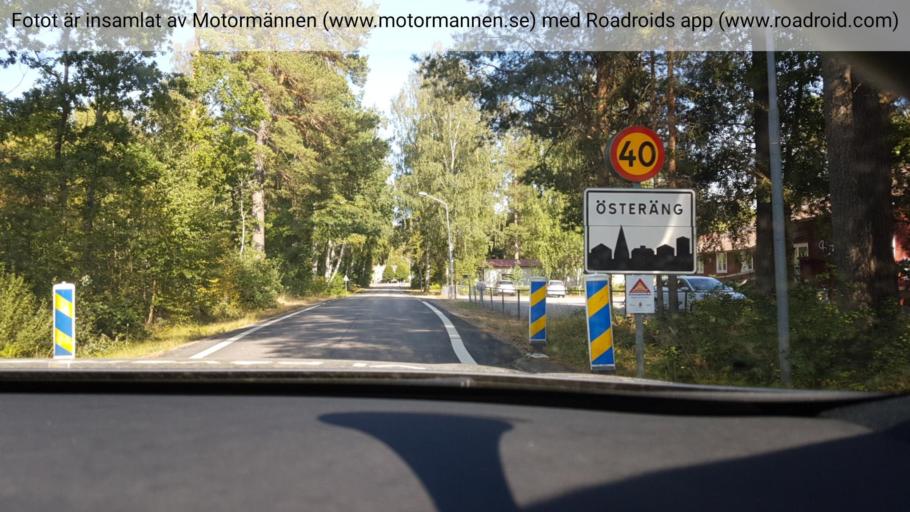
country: SE
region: Vaestra Goetaland
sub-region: Gotene Kommun
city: Goetene
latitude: 58.6365
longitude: 13.5568
